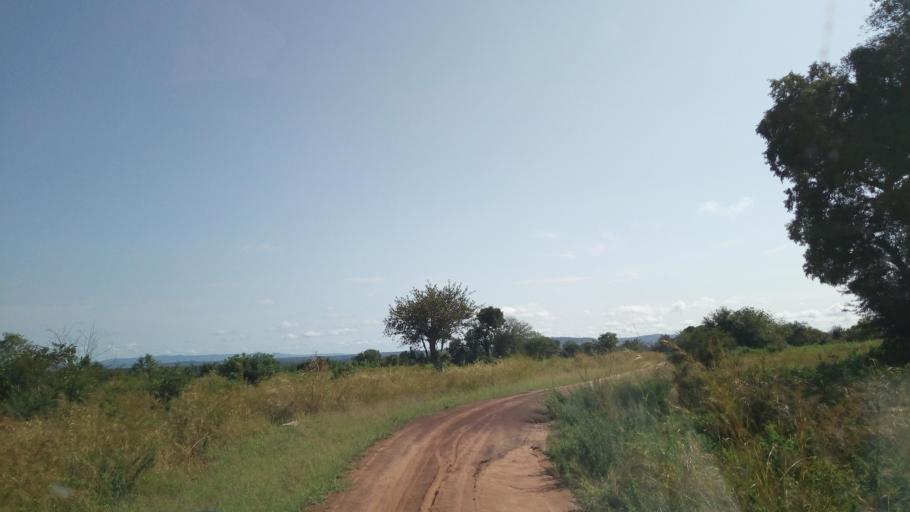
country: UG
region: Northern Region
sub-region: Adjumani District
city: Adjumani
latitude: 3.4593
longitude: 31.8923
